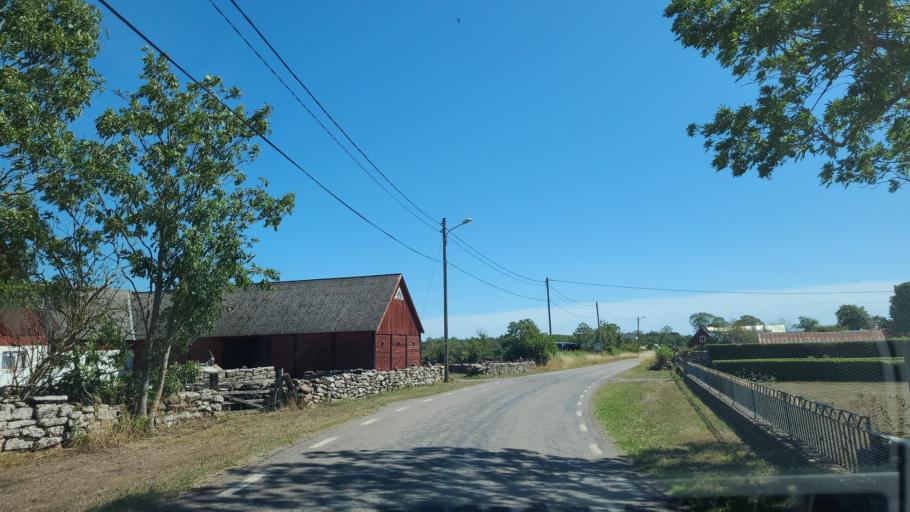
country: SE
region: Kalmar
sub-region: Borgholms Kommun
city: Borgholm
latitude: 56.7692
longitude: 16.6485
